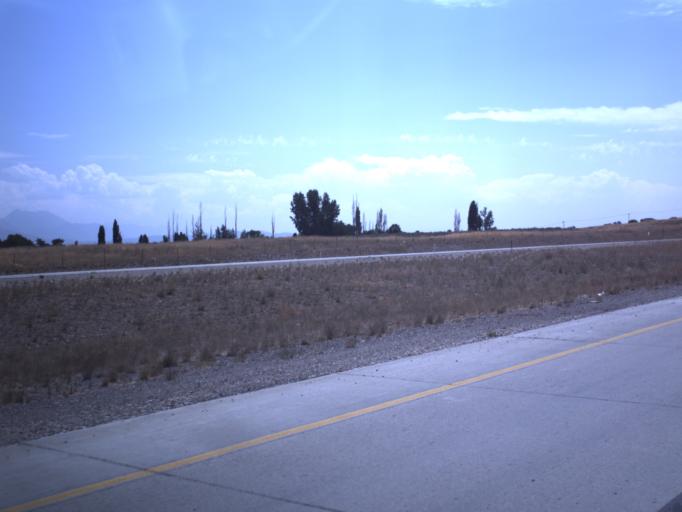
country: US
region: Utah
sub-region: Salt Lake County
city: Oquirrh
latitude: 40.6455
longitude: -112.0453
